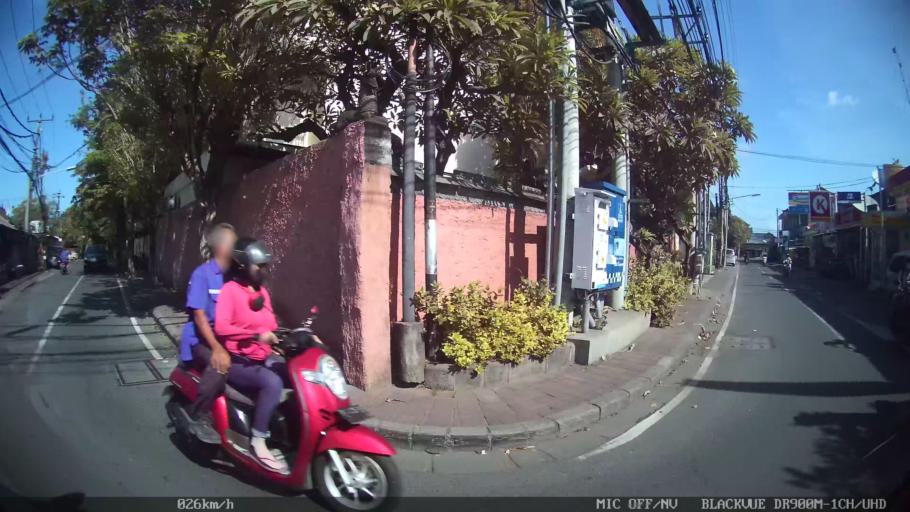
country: ID
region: Bali
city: Jabajero
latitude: -8.7318
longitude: 115.1714
